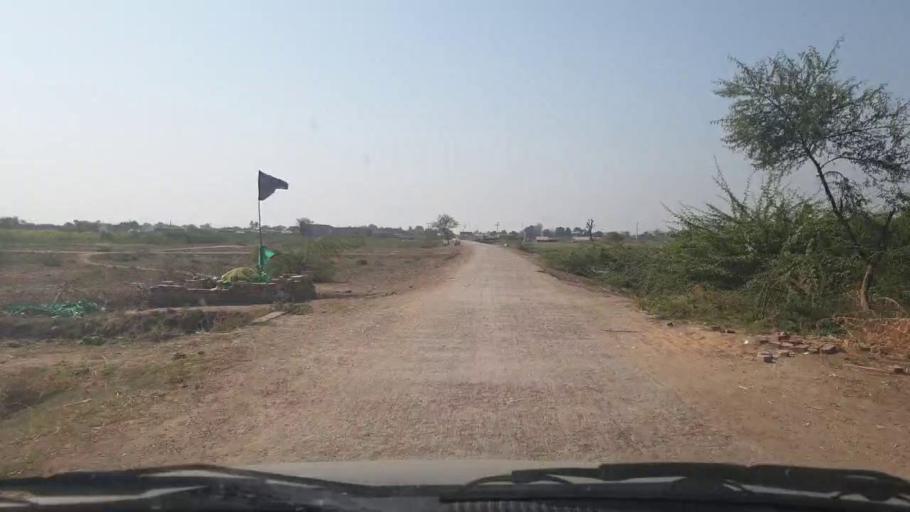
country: PK
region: Sindh
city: Samaro
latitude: 25.2841
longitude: 69.2964
